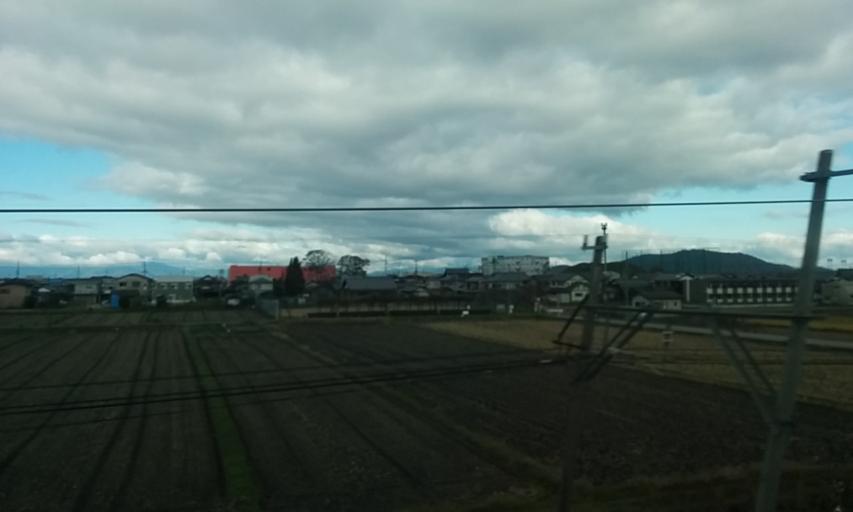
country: JP
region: Shiga Prefecture
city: Youkaichi
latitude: 35.1836
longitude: 136.2194
